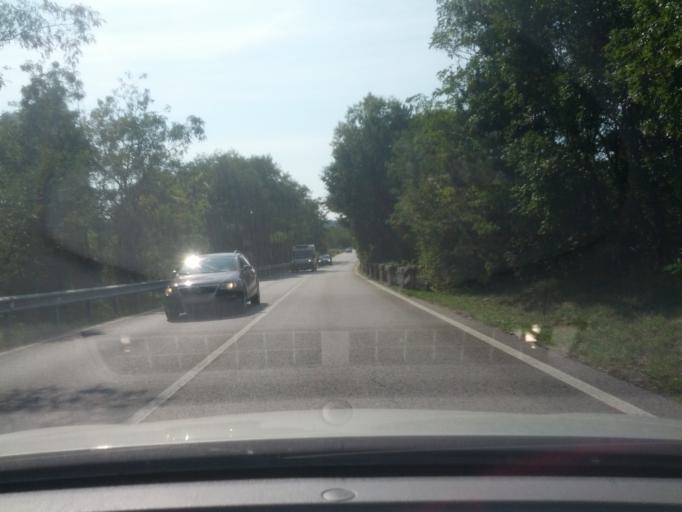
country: IT
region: Friuli Venezia Giulia
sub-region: Provincia di Trieste
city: Zolla
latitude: 45.6945
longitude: 13.8169
